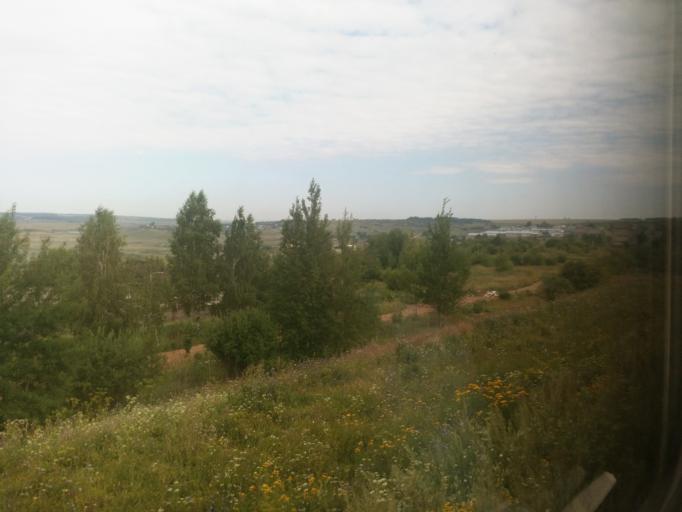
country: RU
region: Tatarstan
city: Mendeleyevsk
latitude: 55.9009
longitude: 52.3321
